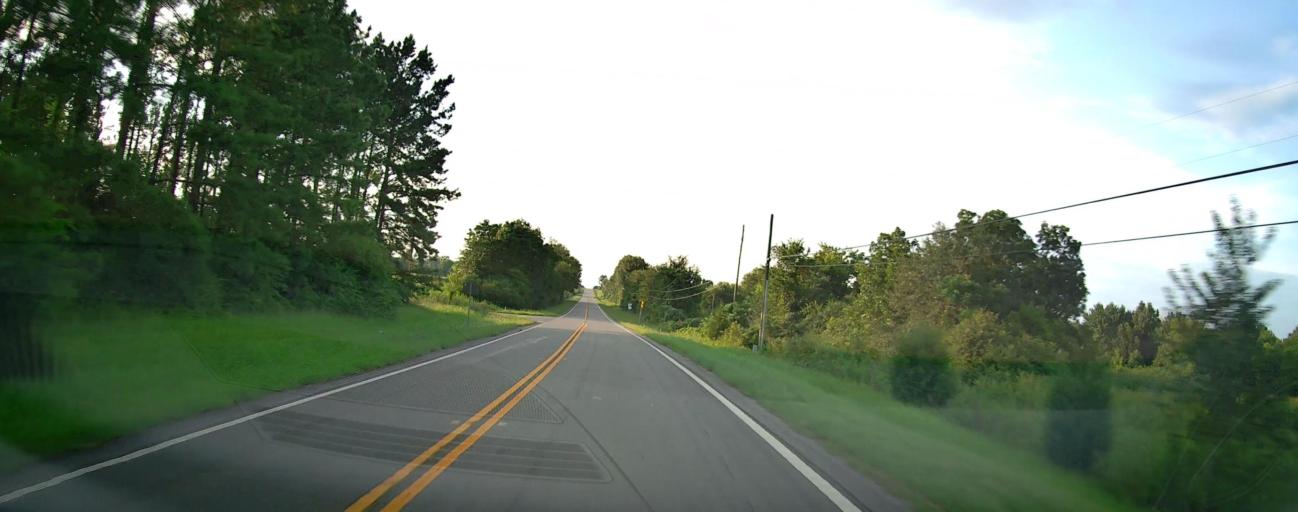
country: US
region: Georgia
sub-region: Taylor County
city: Reynolds
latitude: 32.5882
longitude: -84.0898
